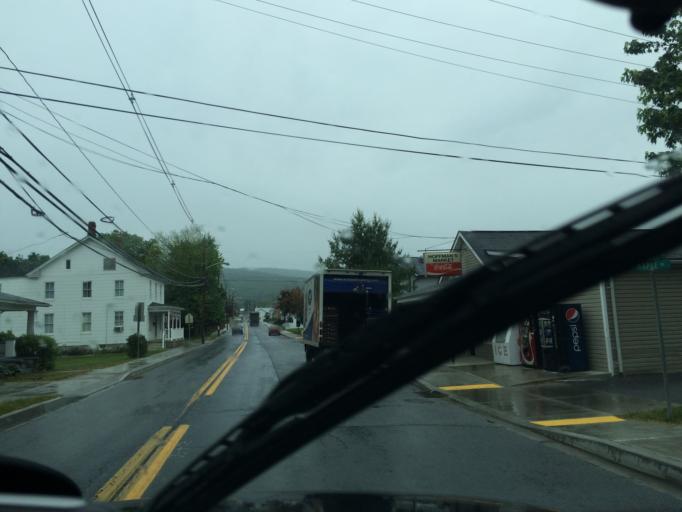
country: US
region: Maryland
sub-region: Frederick County
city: Thurmont
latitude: 39.6213
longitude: -77.4043
